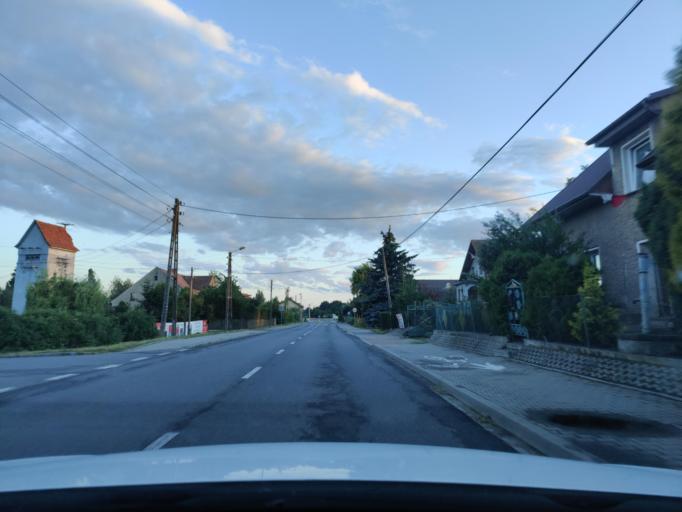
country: PL
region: Opole Voivodeship
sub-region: Powiat nyski
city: Chroscina
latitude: 50.6505
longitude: 17.3847
